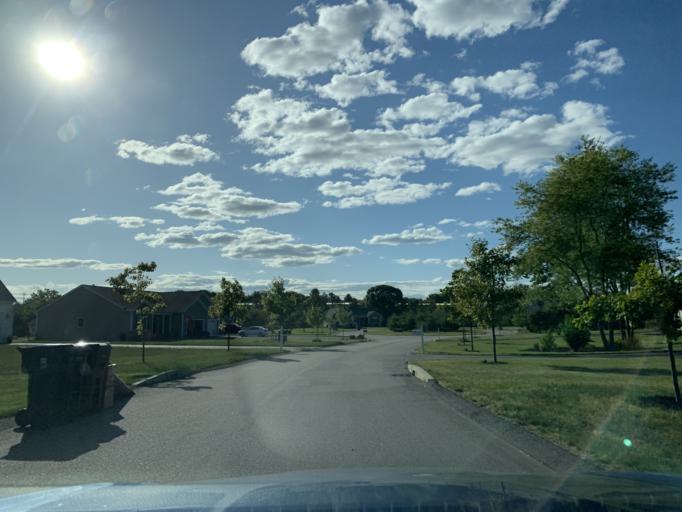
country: US
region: Rhode Island
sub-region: Kent County
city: East Greenwich
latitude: 41.6320
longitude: -71.4621
